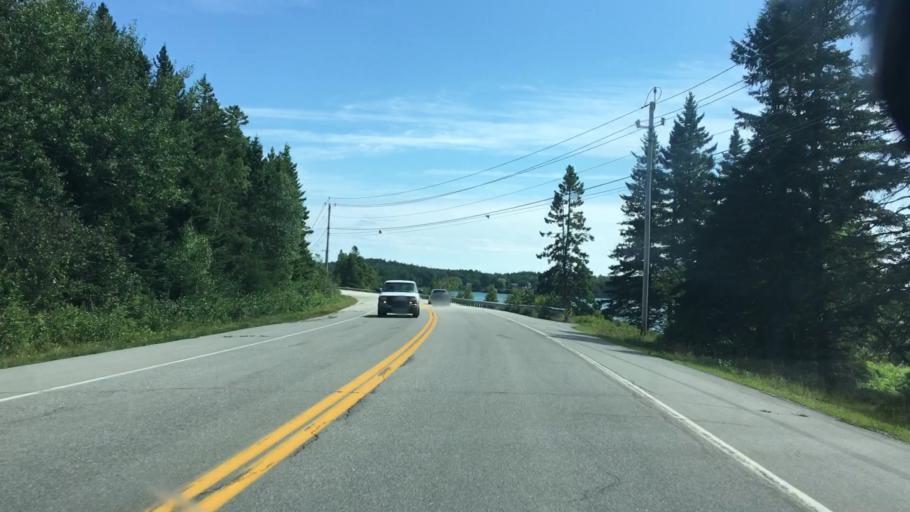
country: US
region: Maine
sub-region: Washington County
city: Eastport
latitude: 44.9413
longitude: -67.0376
